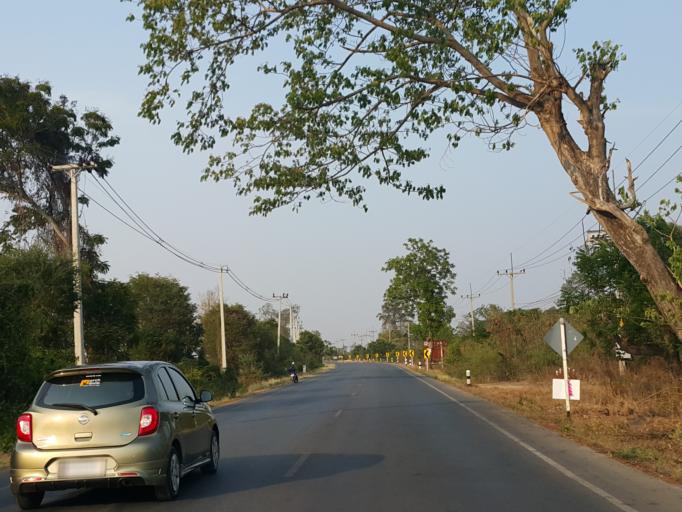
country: TH
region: Chai Nat
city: Sankhaburi
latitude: 15.0697
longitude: 100.1711
